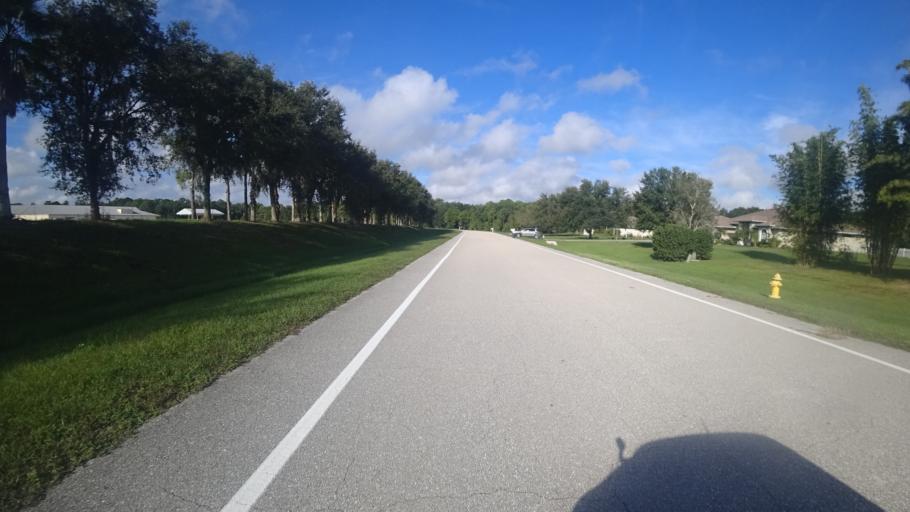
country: US
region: Florida
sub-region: Hillsborough County
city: Sun City Center
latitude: 27.5597
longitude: -82.3660
